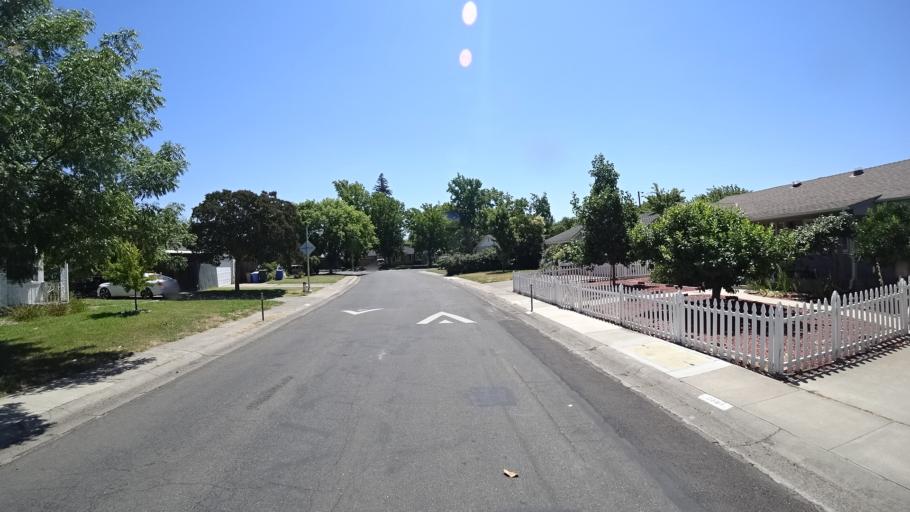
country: US
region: California
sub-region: Sacramento County
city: Parkway
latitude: 38.5330
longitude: -121.4892
